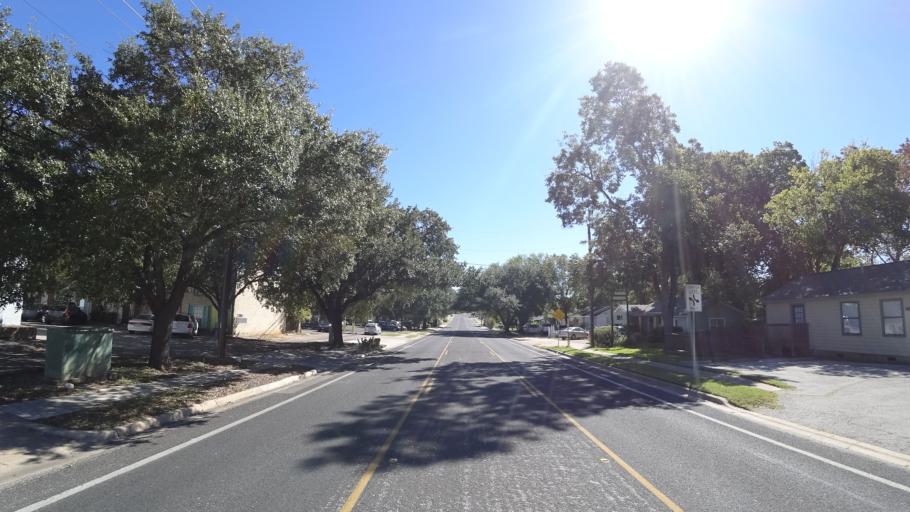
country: US
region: Texas
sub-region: Travis County
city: Austin
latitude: 30.3240
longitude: -97.7424
